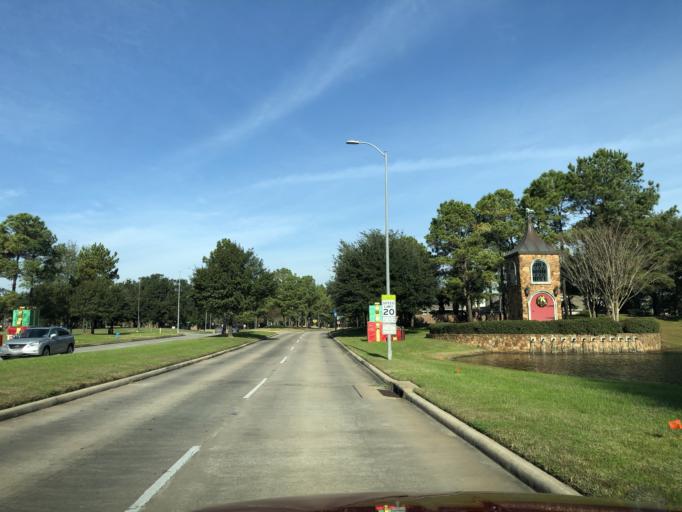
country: US
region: Texas
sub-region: Harris County
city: Tomball
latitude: 30.0274
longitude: -95.5634
